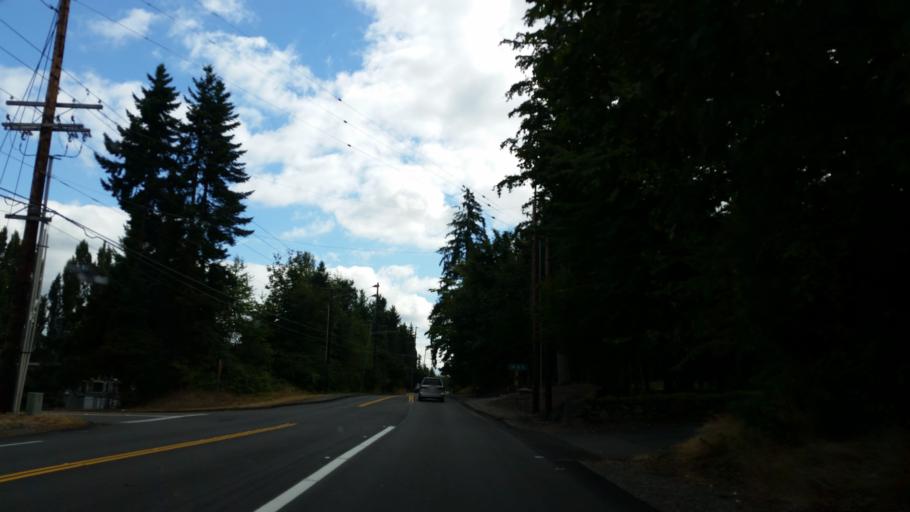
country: US
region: Washington
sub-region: Pierce County
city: Bonney Lake
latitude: 47.2268
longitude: -122.1442
